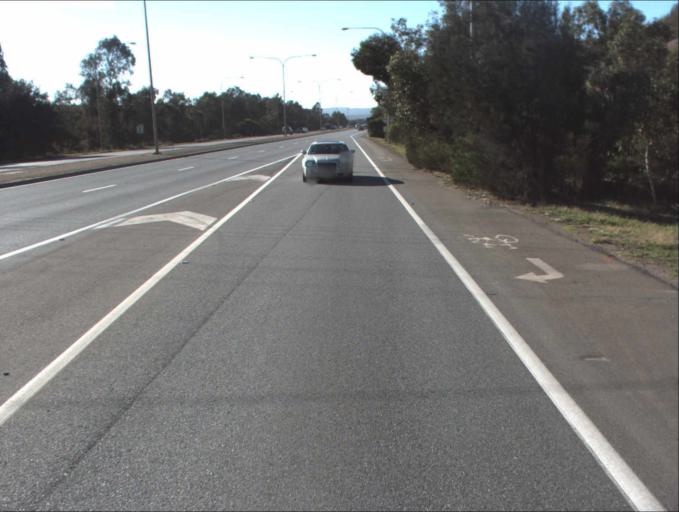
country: AU
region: South Australia
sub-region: Port Adelaide Enfield
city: Alberton
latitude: -34.8336
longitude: 138.5499
